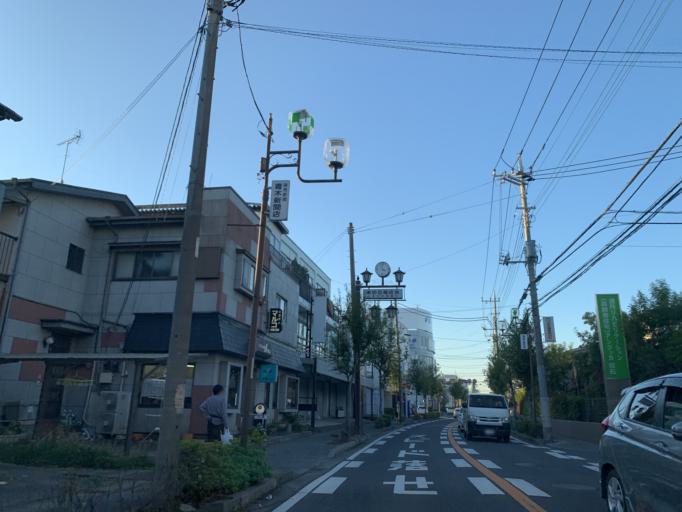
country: JP
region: Chiba
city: Nagareyama
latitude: 35.8866
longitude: 139.9198
